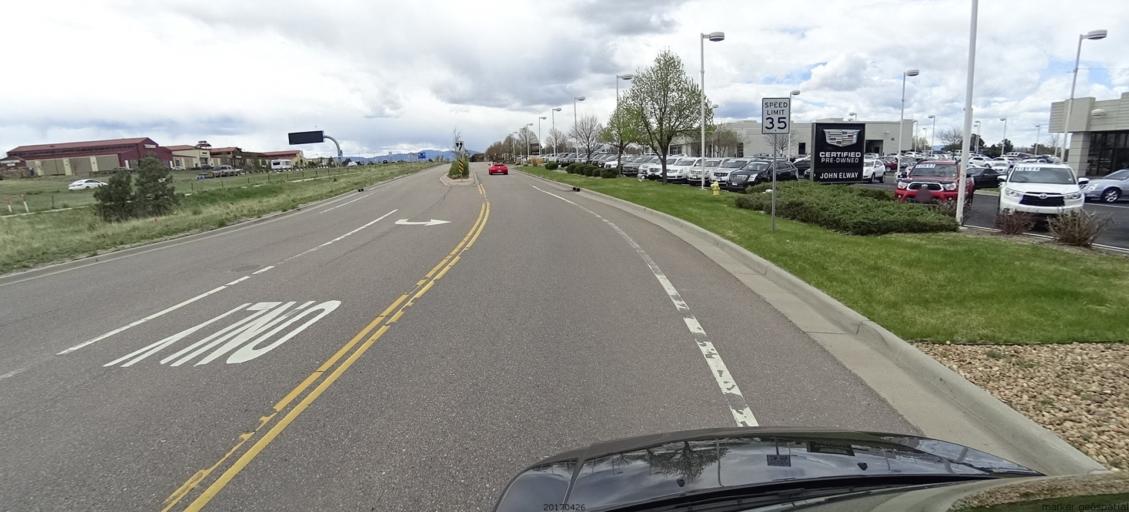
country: US
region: Colorado
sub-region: Douglas County
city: Acres Green
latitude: 39.5648
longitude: -104.8913
